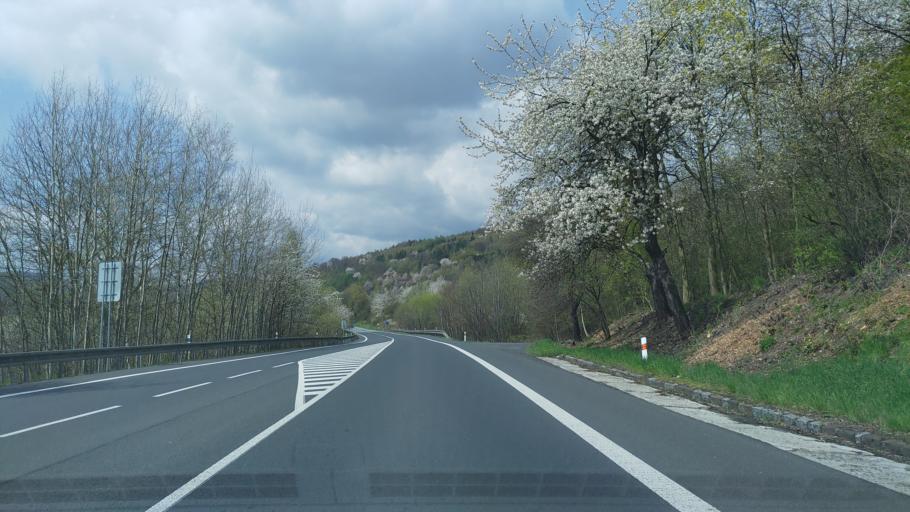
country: CZ
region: Ustecky
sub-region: Okres Chomutov
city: Perstejn
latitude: 50.3747
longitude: 13.1075
